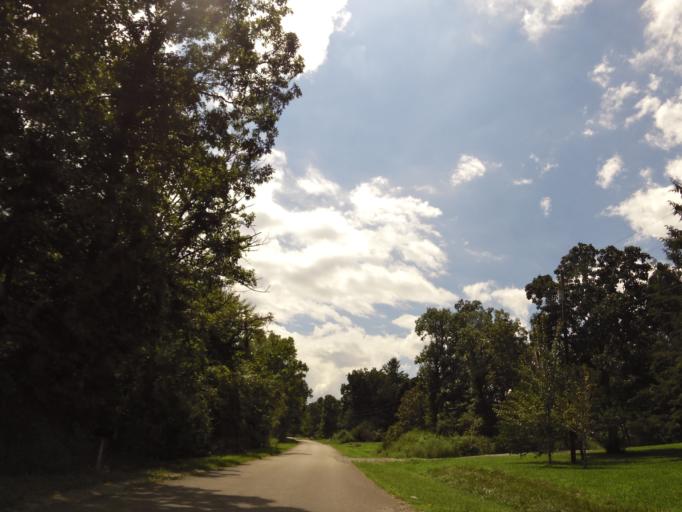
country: US
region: Tennessee
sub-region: Roane County
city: Rockwood
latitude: 35.8890
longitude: -84.7990
